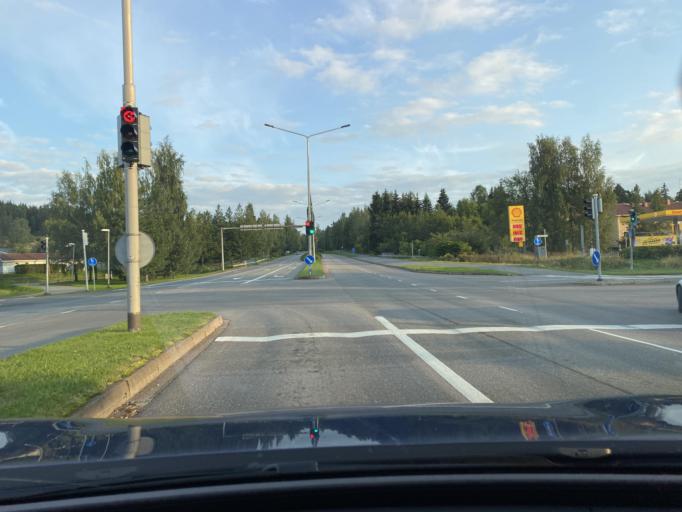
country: FI
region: Kymenlaakso
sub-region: Kouvola
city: Kouvola
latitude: 60.9017
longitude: 26.6303
